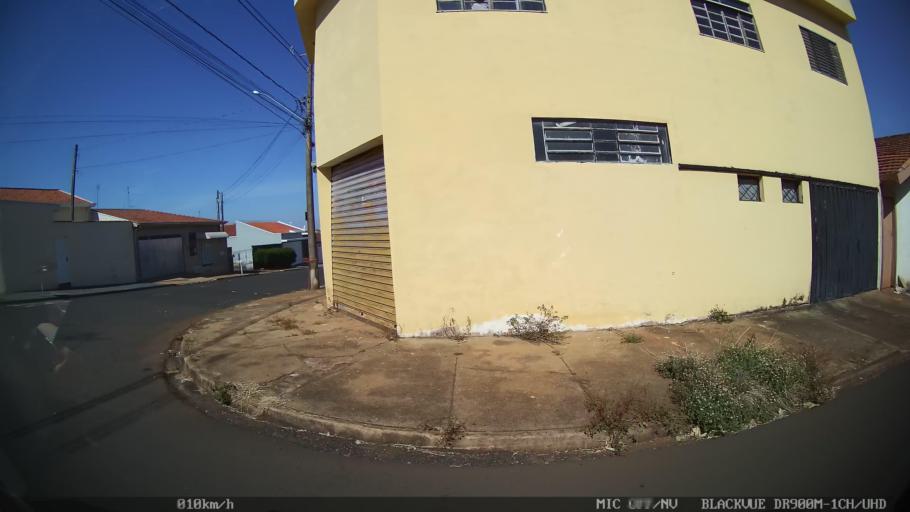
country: BR
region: Sao Paulo
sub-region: Batatais
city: Batatais
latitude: -20.8888
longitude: -47.5756
